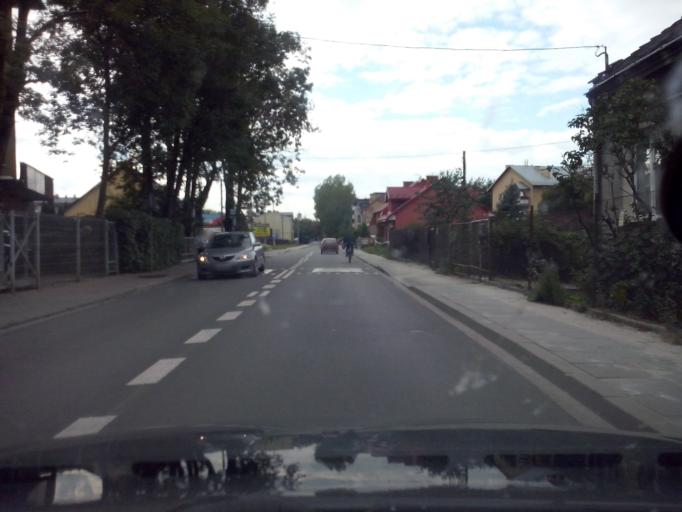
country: PL
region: Lesser Poland Voivodeship
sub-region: Krakow
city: Krakow
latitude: 50.0425
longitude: 19.9904
